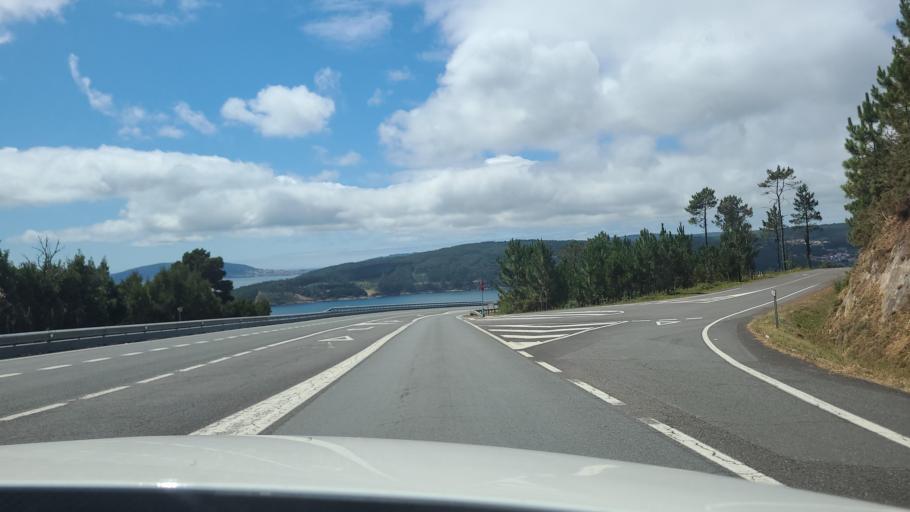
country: ES
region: Galicia
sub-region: Provincia da Coruna
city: Corcubion
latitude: 42.9234
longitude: -9.1590
